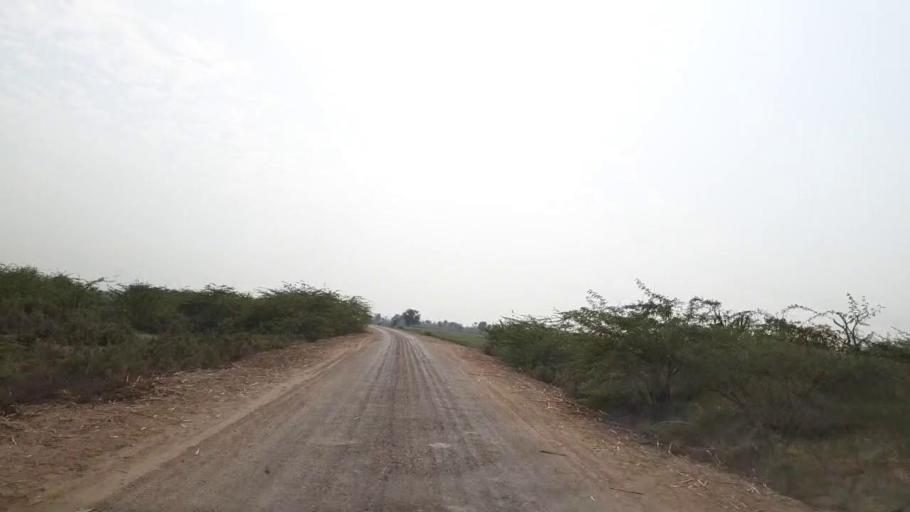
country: PK
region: Sindh
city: Mirpur Khas
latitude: 25.5383
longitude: 69.1584
